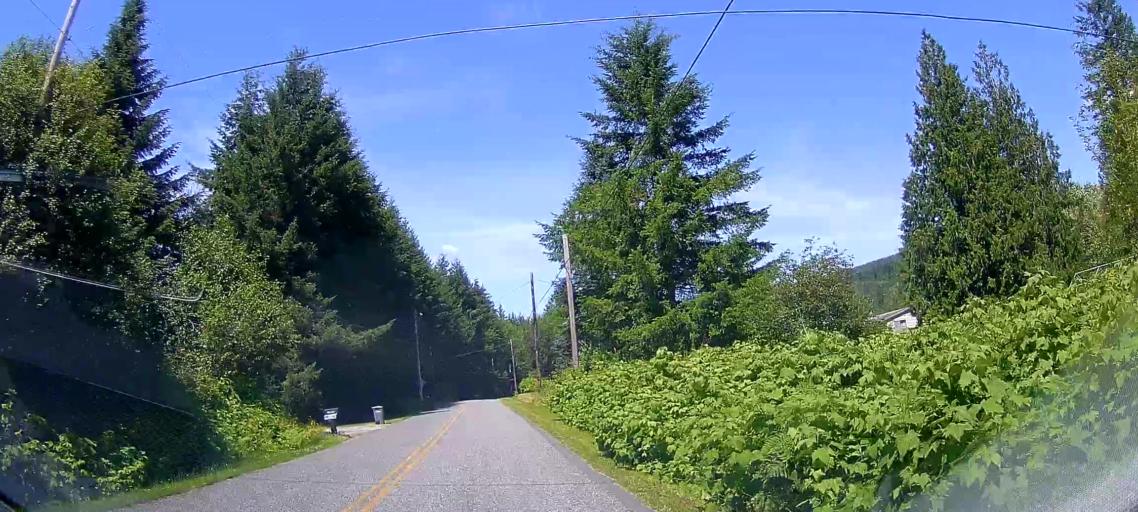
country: US
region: Washington
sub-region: Skagit County
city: Burlington
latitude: 48.5953
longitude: -122.3172
